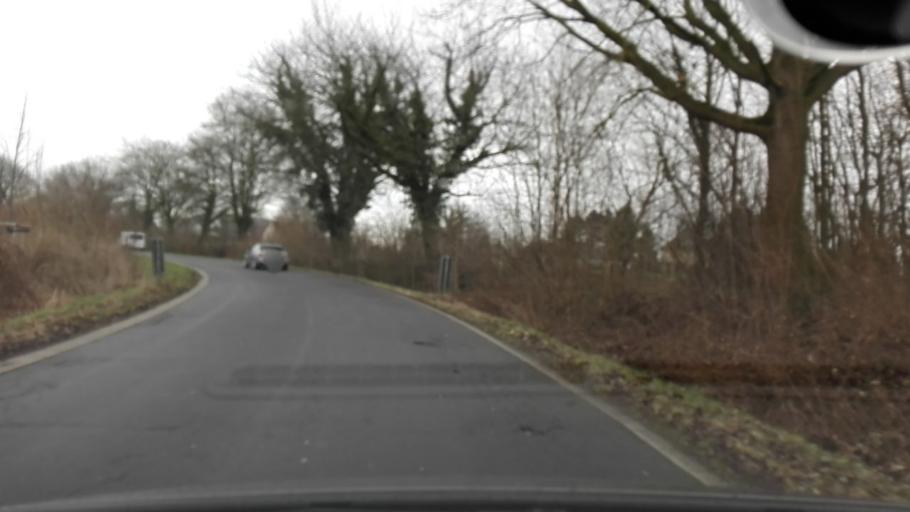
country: DE
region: North Rhine-Westphalia
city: Kamen
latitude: 51.5783
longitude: 7.6444
